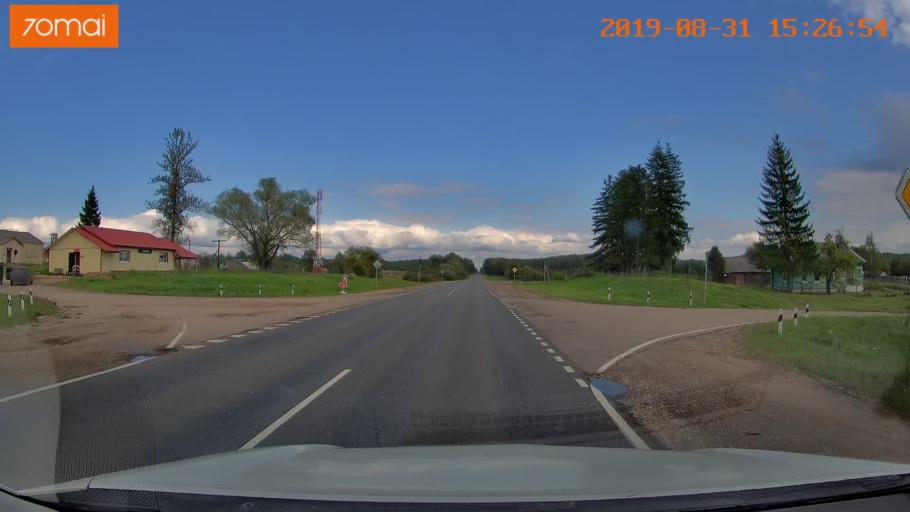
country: RU
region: Kaluga
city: Baryatino
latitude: 54.5528
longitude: 34.5475
